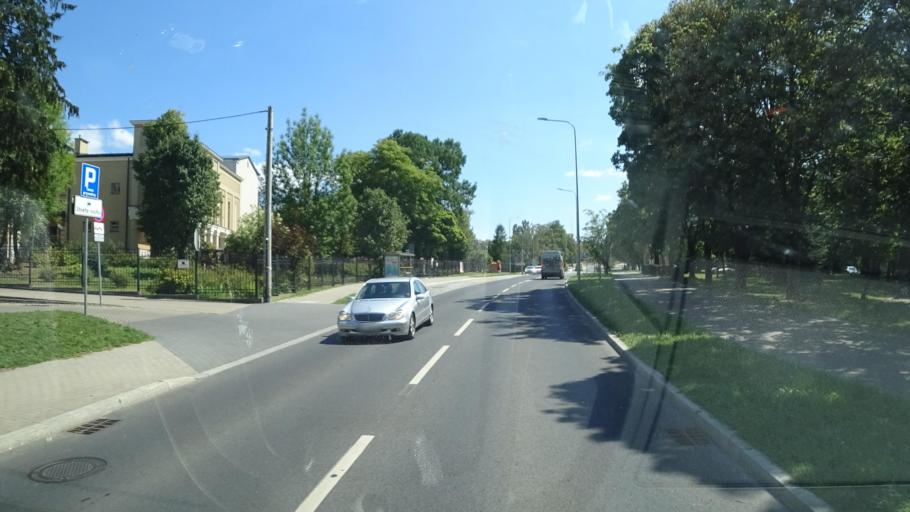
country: PL
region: Podlasie
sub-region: Lomza
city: Lomza
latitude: 53.1771
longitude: 22.0759
